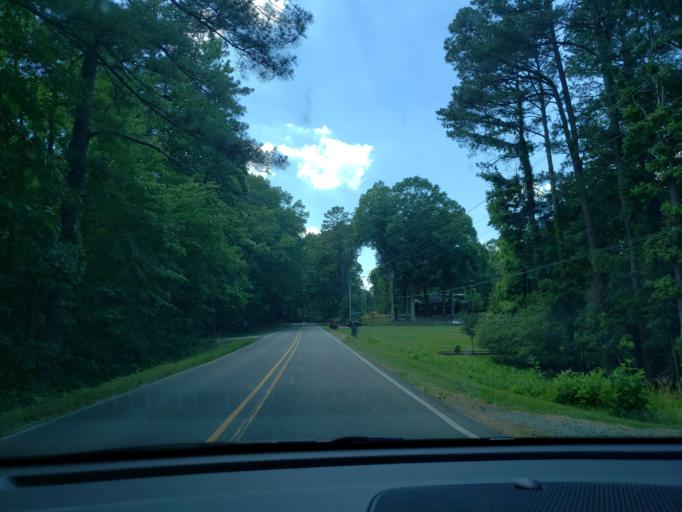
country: US
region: North Carolina
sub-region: Orange County
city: Chapel Hill
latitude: 35.9997
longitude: -79.0200
